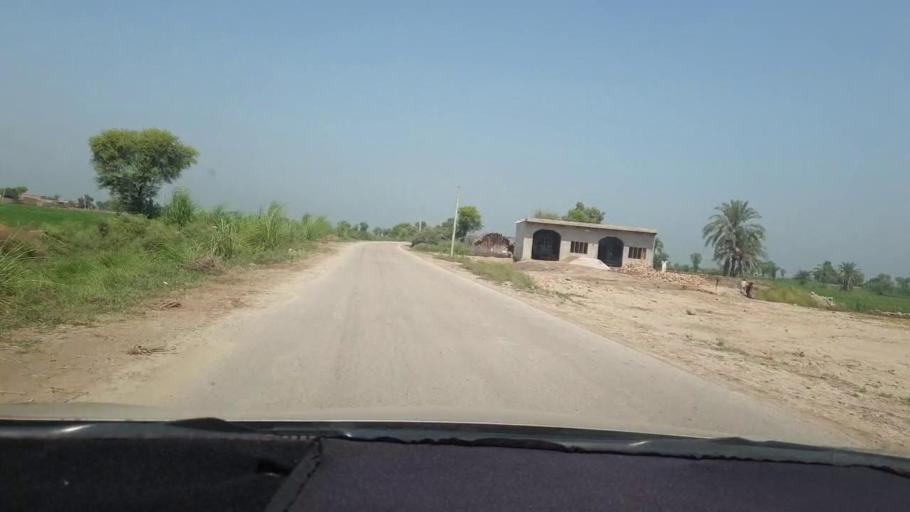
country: PK
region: Sindh
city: Miro Khan
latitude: 27.8177
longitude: 68.0254
